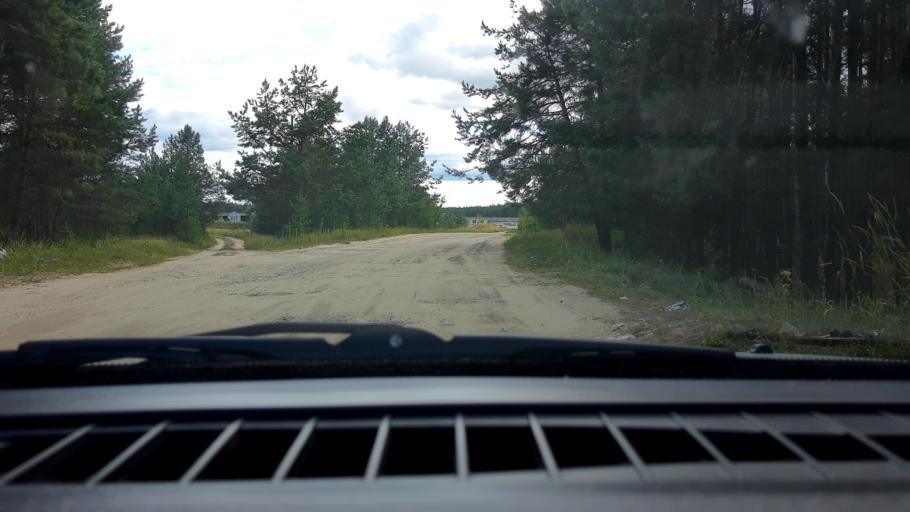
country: RU
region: Nizjnij Novgorod
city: Lukino
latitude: 56.3870
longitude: 43.7096
